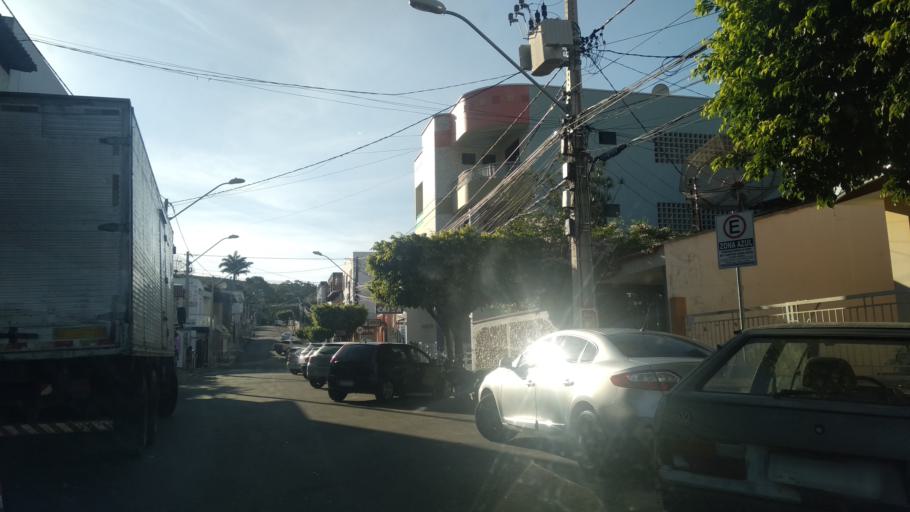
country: BR
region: Bahia
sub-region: Caetite
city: Caetite
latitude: -14.0689
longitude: -42.4894
